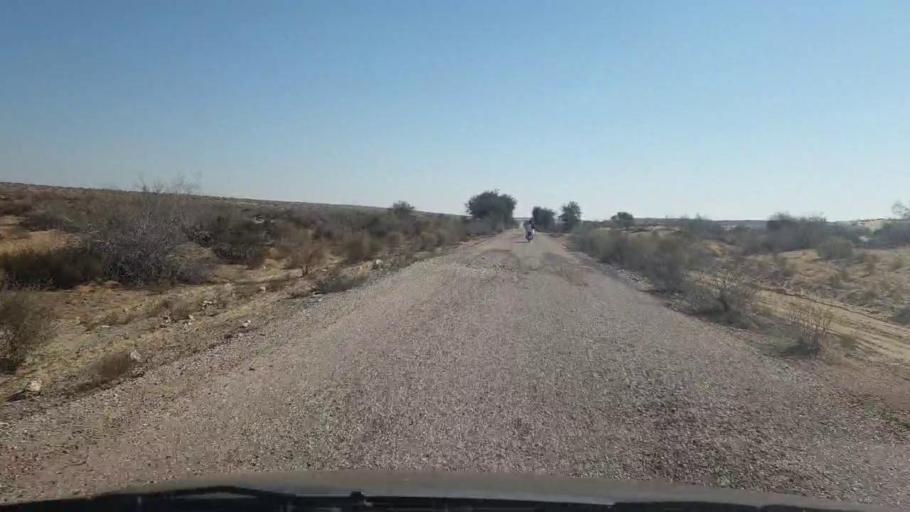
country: PK
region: Sindh
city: Bozdar
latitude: 27.0349
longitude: 68.6980
